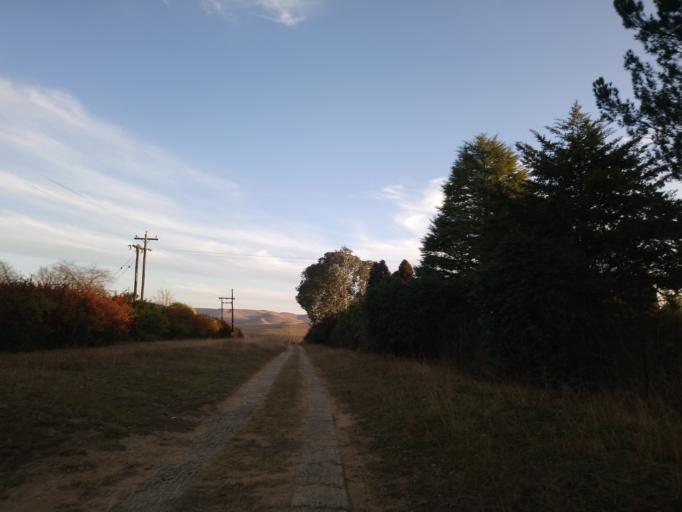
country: ZA
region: KwaZulu-Natal
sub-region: uMgungundlovu District Municipality
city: Mooirivier
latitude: -29.3297
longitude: 29.9199
